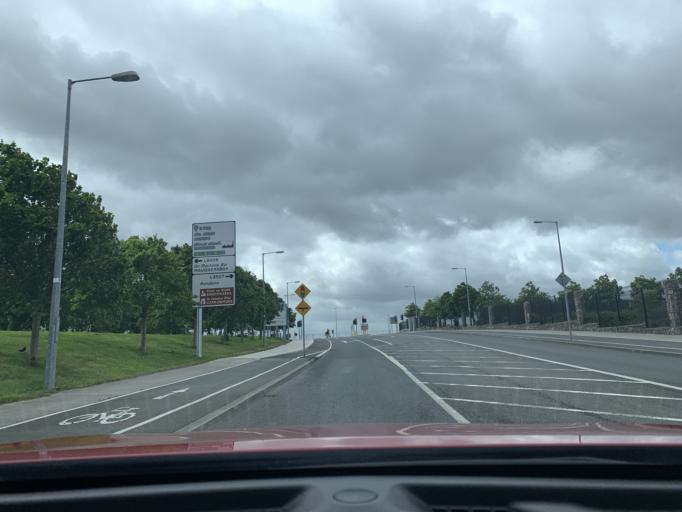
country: IE
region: Connaught
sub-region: Sligo
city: Sligo
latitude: 54.2673
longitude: -8.5030
